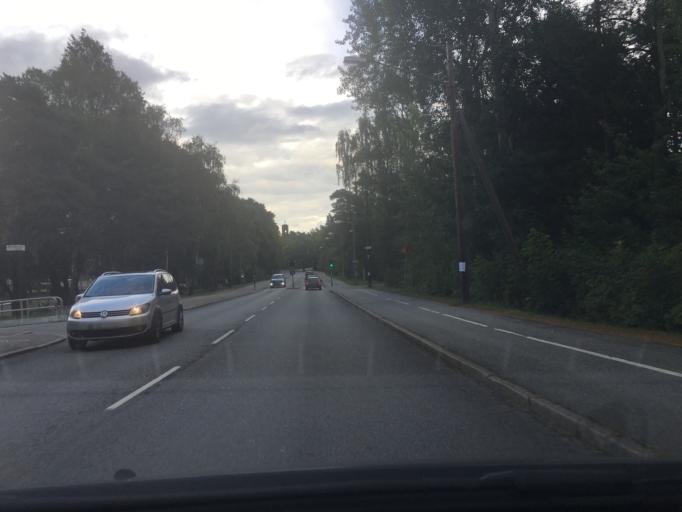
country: SE
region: Stockholm
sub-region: Stockholms Kommun
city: Bromma
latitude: 59.3283
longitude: 17.9581
